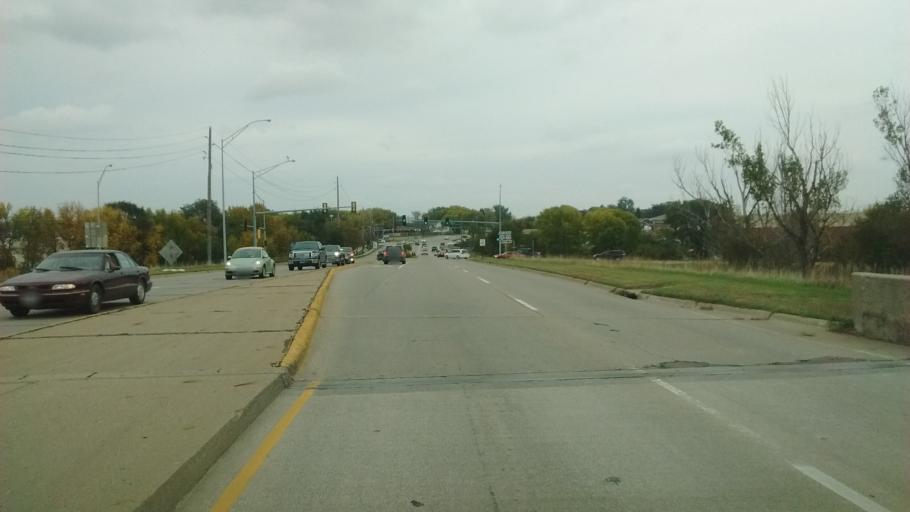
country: US
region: Iowa
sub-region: Woodbury County
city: Sergeant Bluff
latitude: 42.4440
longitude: -96.3471
